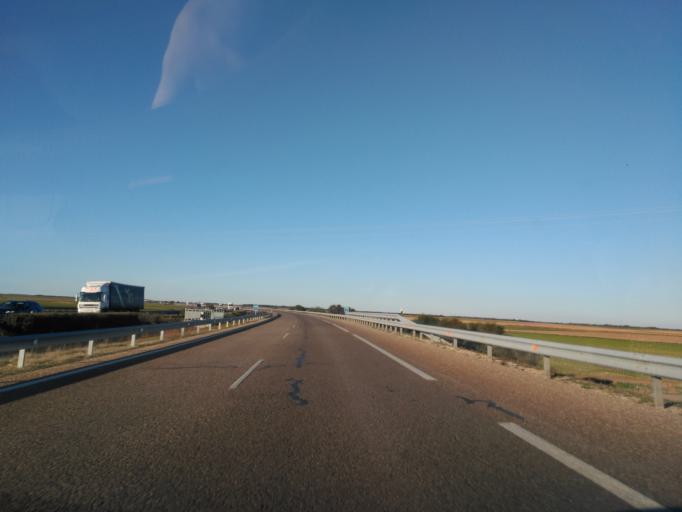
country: ES
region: Castille and Leon
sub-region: Provincia de Salamanca
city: Pajares de la Laguna
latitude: 41.1094
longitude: -5.4909
